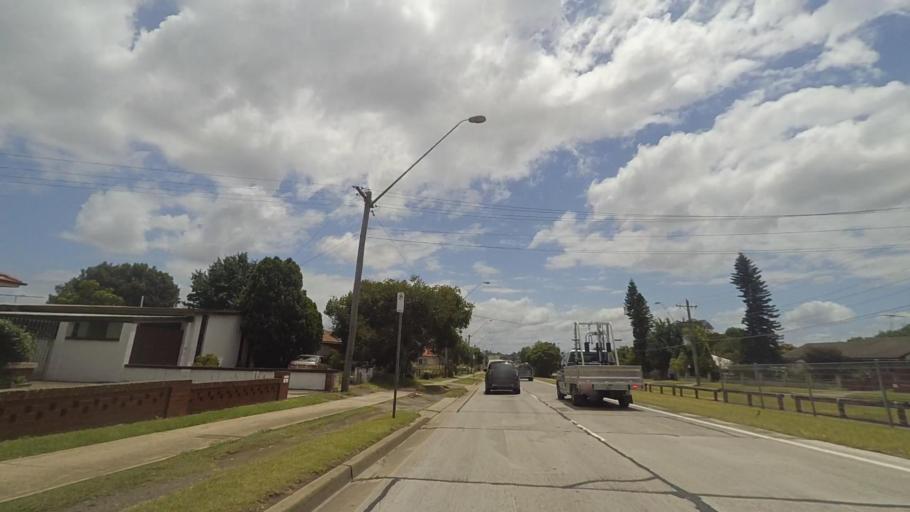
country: AU
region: New South Wales
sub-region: Fairfield
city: Cabramatta West
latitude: -33.8957
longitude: 150.9218
